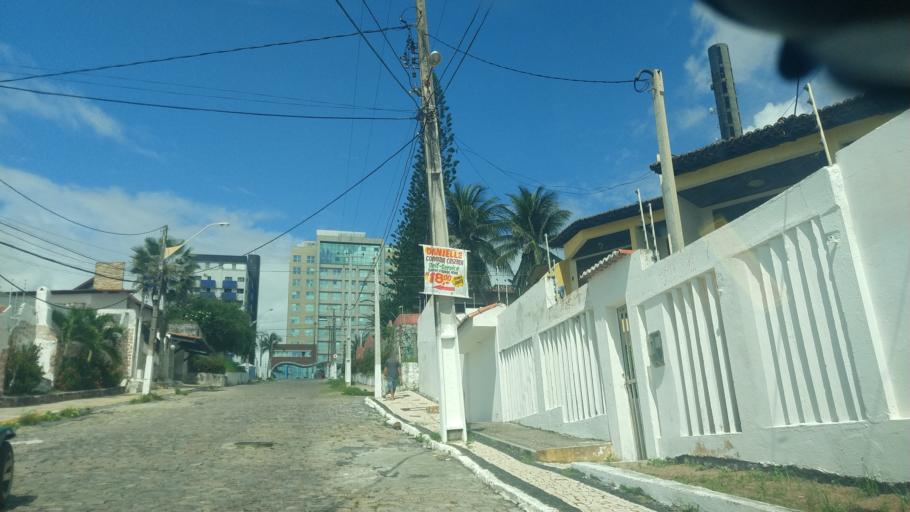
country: BR
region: Rio Grande do Norte
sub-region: Natal
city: Natal
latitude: -5.8719
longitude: -35.1791
